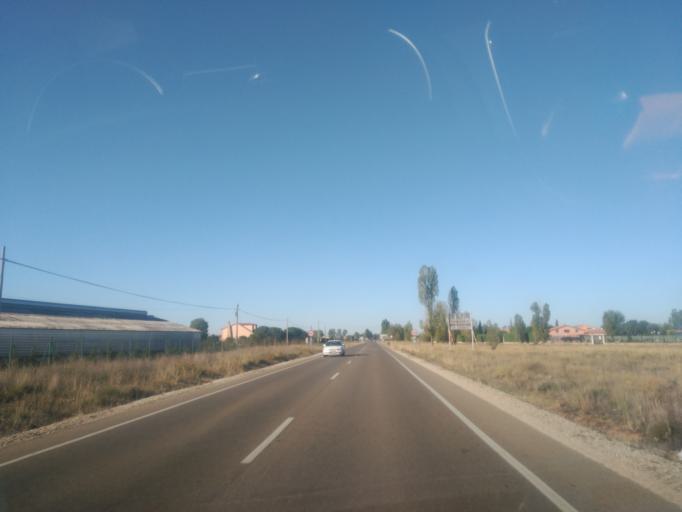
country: ES
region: Castille and Leon
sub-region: Provincia de Burgos
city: Fresnillo de las Duenas
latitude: 41.6845
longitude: -3.6272
